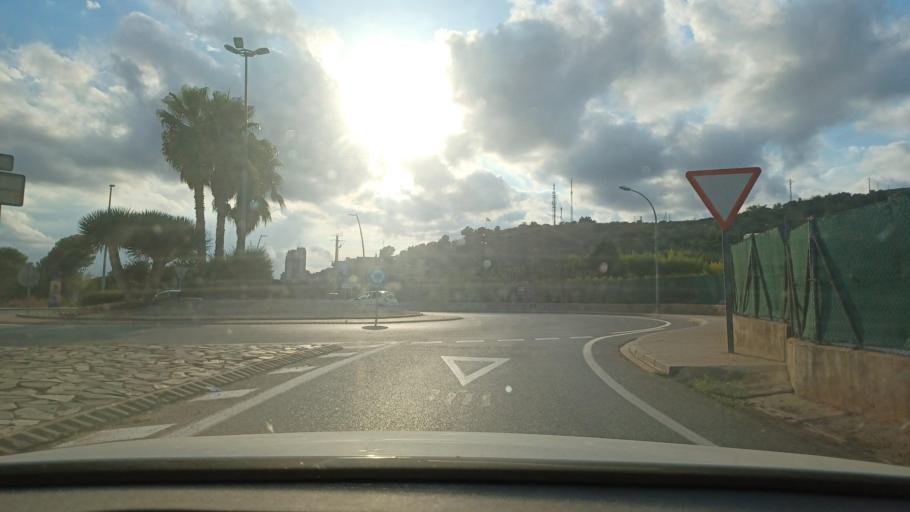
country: ES
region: Catalonia
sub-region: Provincia de Tarragona
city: Alcanar
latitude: 40.5445
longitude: 0.4905
